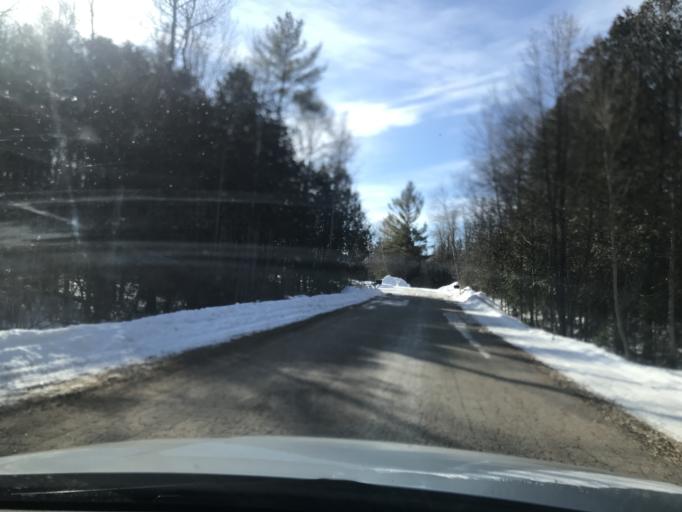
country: US
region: Wisconsin
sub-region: Oconto County
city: Gillett
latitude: 44.9585
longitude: -88.2754
